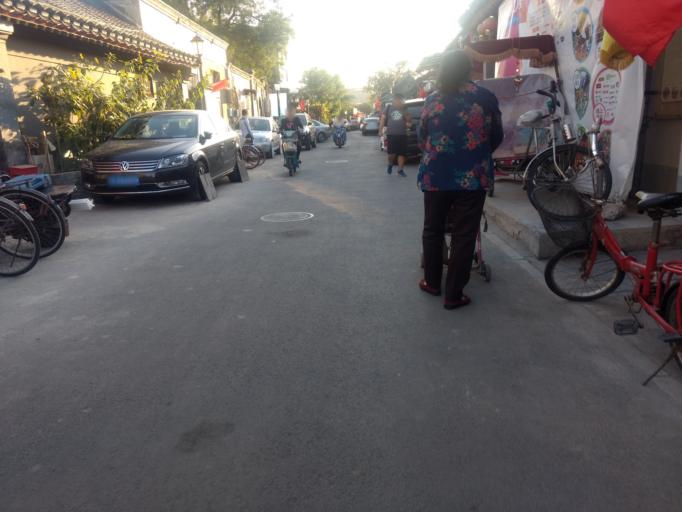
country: CN
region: Beijing
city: Beijing
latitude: 39.8913
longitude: 116.3816
